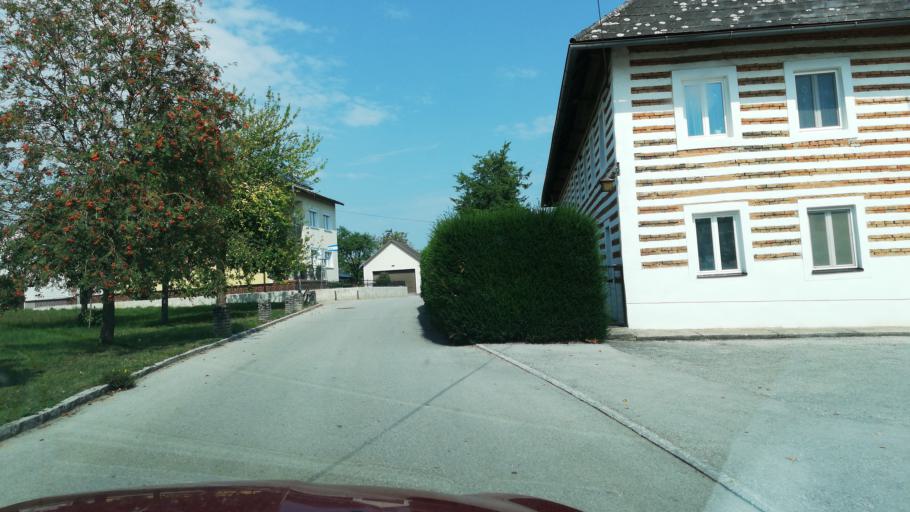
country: AT
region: Upper Austria
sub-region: Politischer Bezirk Steyr-Land
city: Sierning
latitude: 48.0507
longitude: 14.3068
